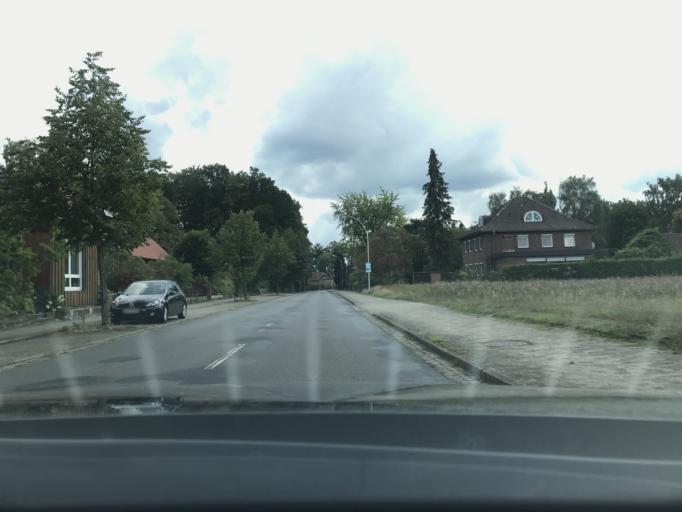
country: DE
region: Lower Saxony
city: Suderburg
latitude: 52.8969
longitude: 10.4423
